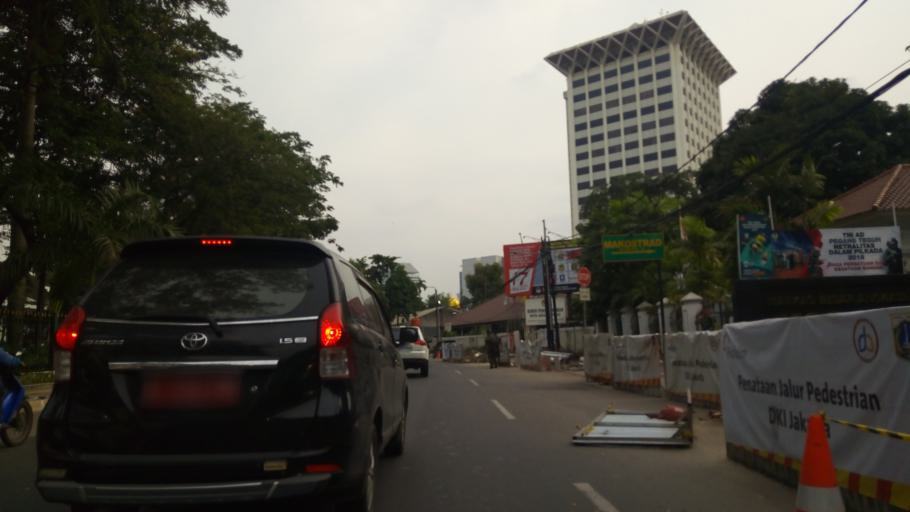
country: ID
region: Jakarta Raya
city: Jakarta
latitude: -6.1741
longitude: 106.8332
